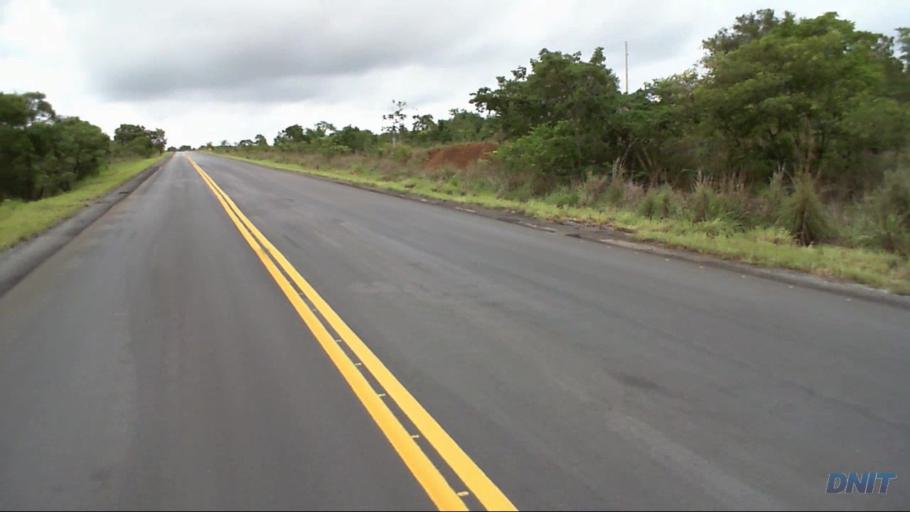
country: BR
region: Goias
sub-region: Padre Bernardo
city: Padre Bernardo
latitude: -15.2148
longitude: -48.5875
